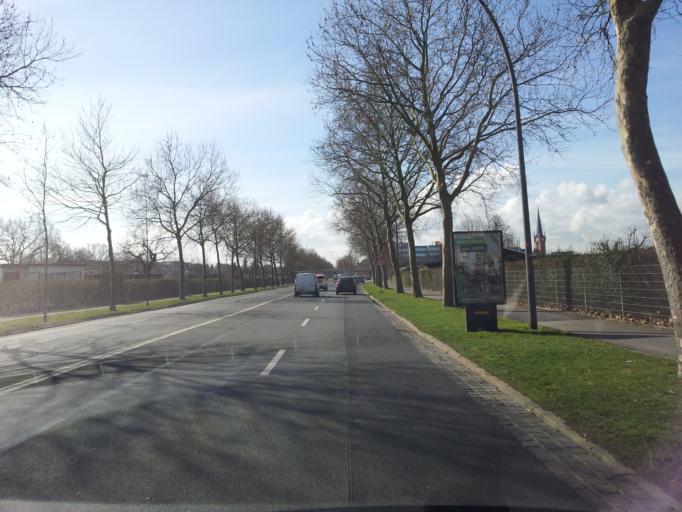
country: DE
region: Saxony
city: Albertstadt
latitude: 51.0786
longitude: 13.7394
